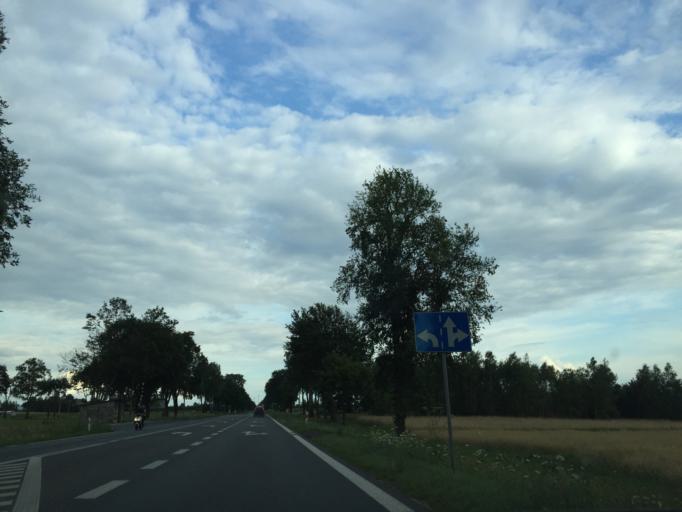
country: PL
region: Lublin Voivodeship
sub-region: Powiat lubartowski
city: Firlej
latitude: 51.5841
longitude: 22.4868
